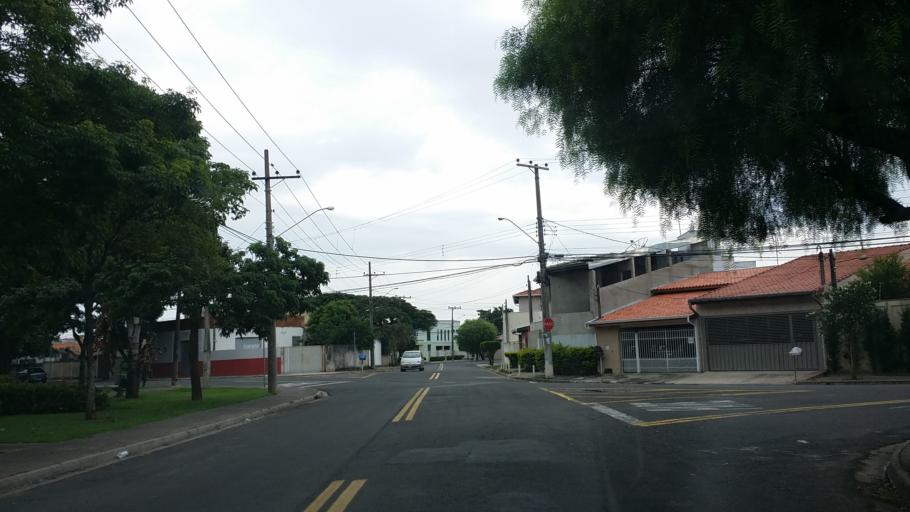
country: BR
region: Sao Paulo
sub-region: Indaiatuba
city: Indaiatuba
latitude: -23.1098
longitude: -47.2175
